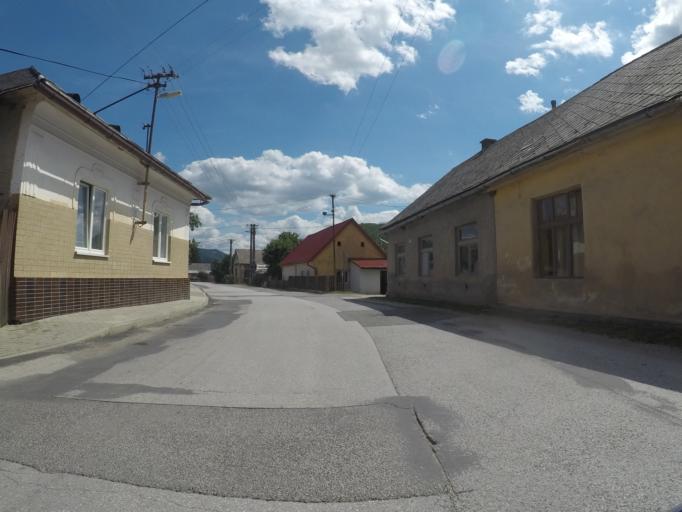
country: SK
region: Banskobystricky
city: Revuca
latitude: 48.7391
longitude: 20.0482
